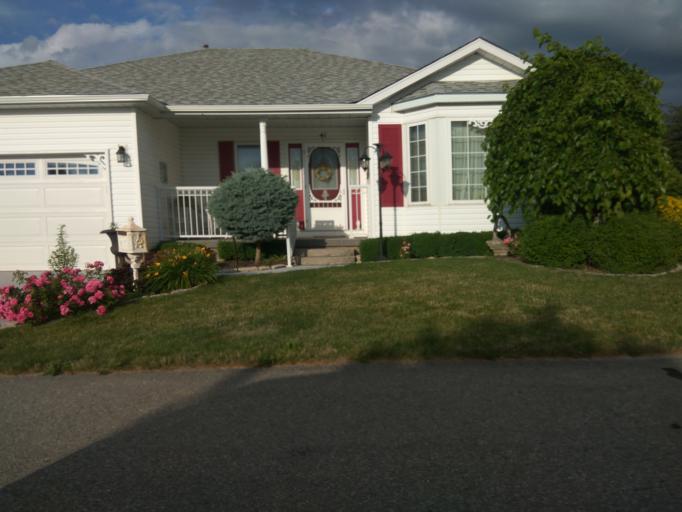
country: CA
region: Ontario
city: Kitchener
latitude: 43.3756
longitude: -80.6864
